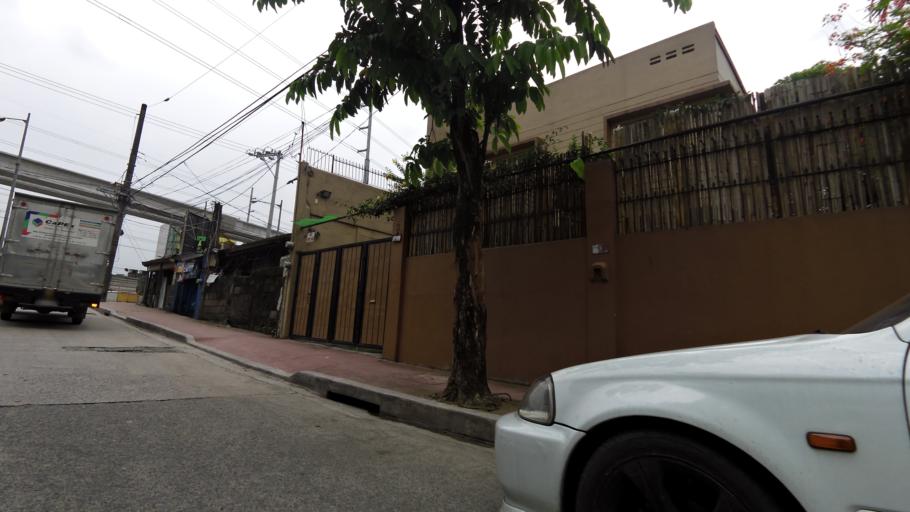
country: PH
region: Metro Manila
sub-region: Marikina
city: Calumpang
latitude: 14.6217
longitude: 121.1041
